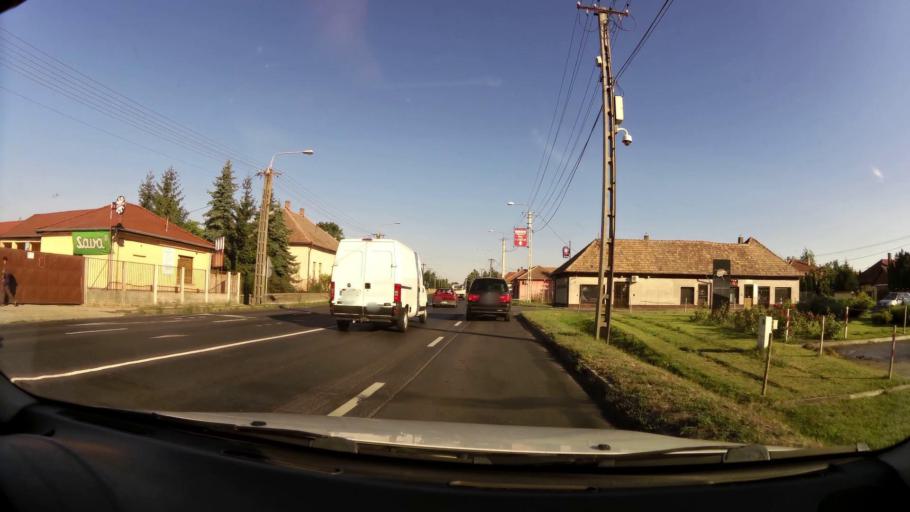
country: HU
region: Pest
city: Pilis
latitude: 47.2867
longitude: 19.5464
